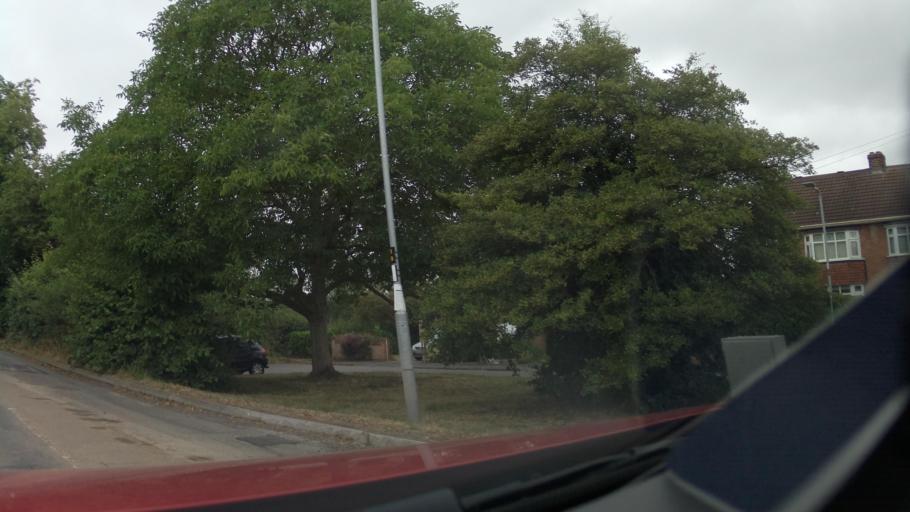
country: GB
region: England
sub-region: Leicestershire
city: Ashby de la Zouch
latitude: 52.7389
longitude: -1.4860
